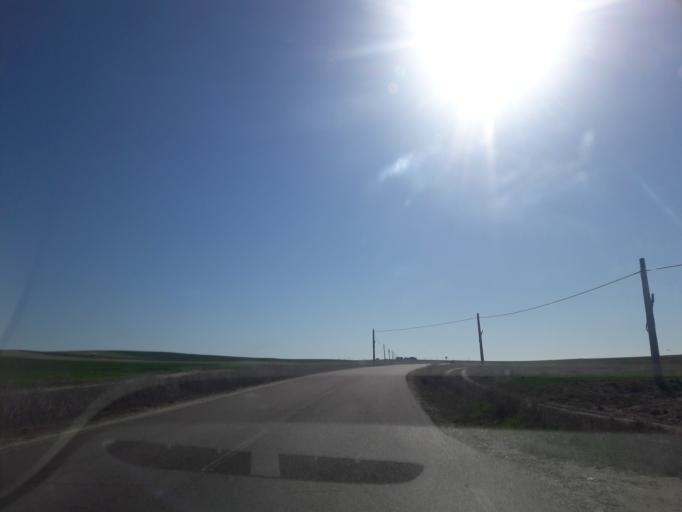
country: ES
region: Castille and Leon
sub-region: Provincia de Salamanca
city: Tordillos
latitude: 40.8508
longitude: -5.3269
